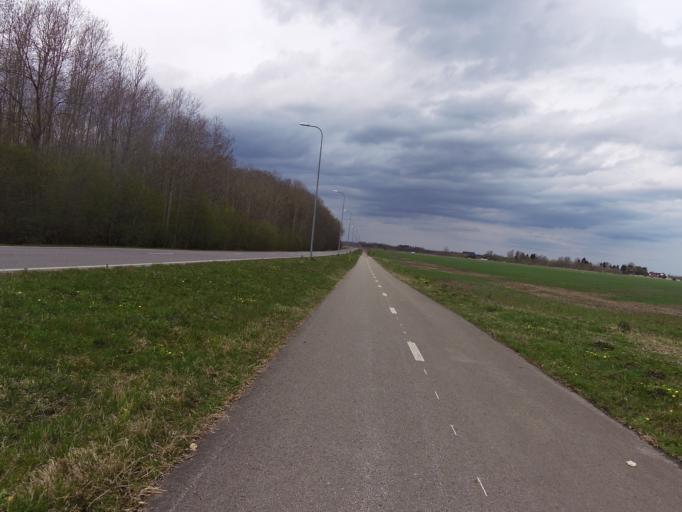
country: EE
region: Harju
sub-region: Kiili vald
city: Kiili
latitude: 59.3683
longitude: 24.8231
